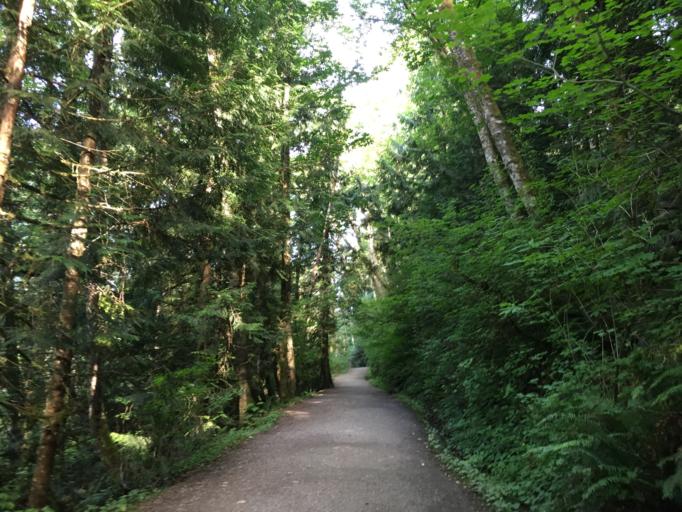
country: US
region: Washington
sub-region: Whatcom County
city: Geneva
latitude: 48.6979
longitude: -122.4448
